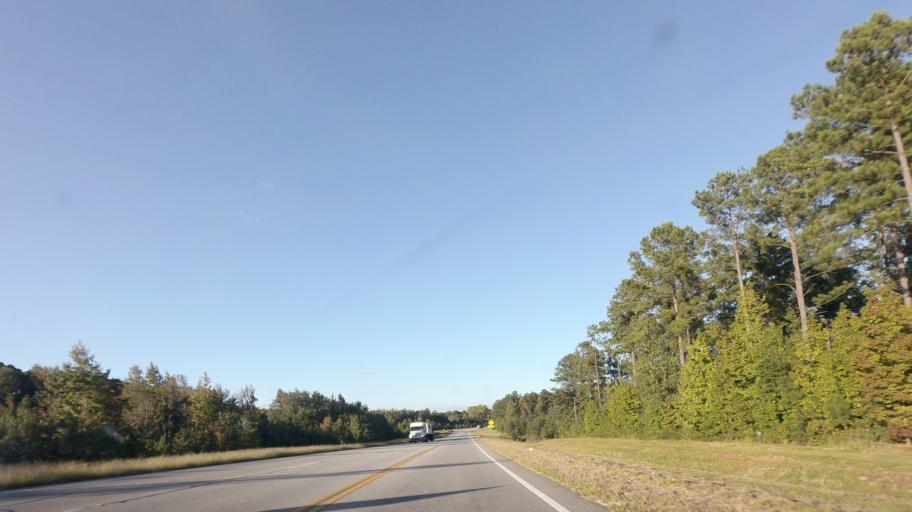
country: US
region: Georgia
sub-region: Spalding County
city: East Griffin
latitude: 33.2897
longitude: -84.1967
